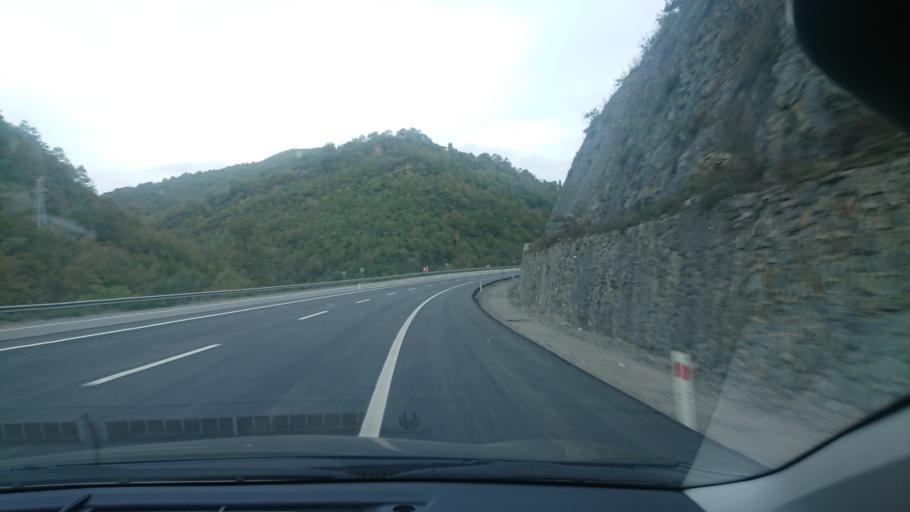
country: TR
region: Zonguldak
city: Beycuma
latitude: 41.3875
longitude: 31.9369
